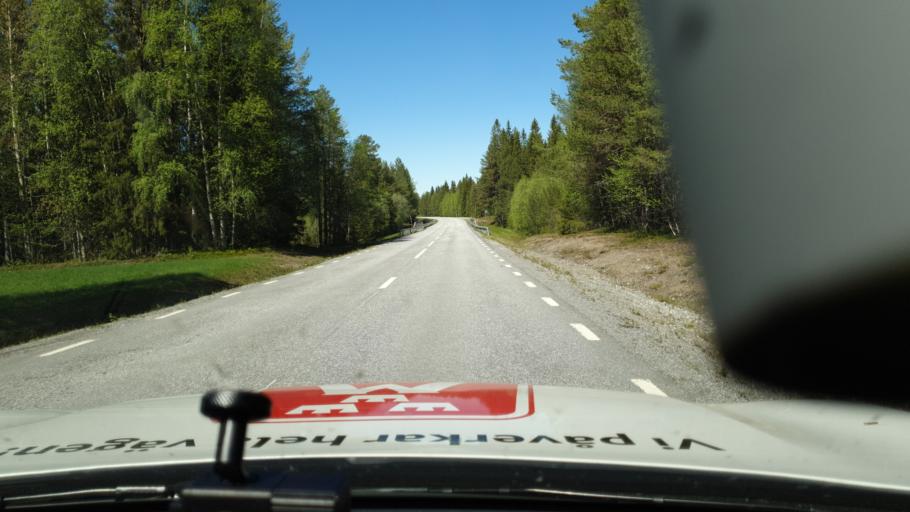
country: SE
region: Vaesterbotten
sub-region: Storumans Kommun
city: Storuman
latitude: 65.1971
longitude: 17.0079
